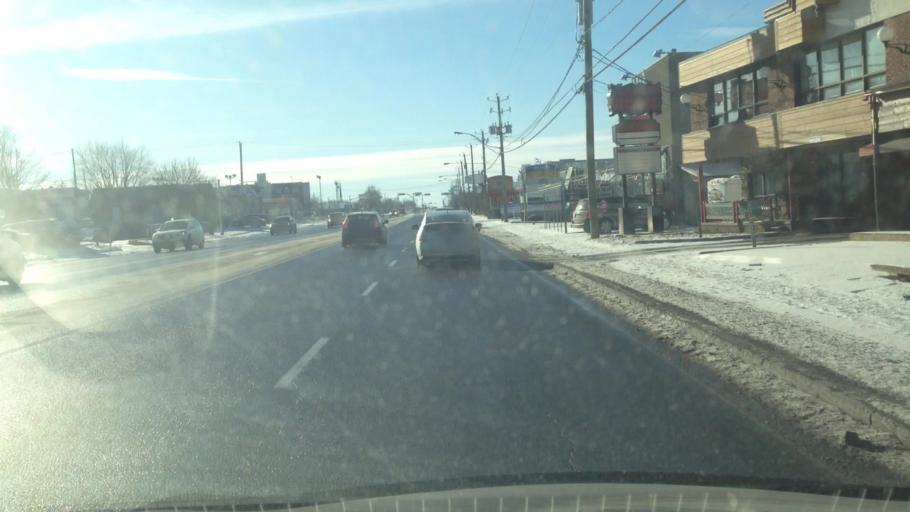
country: CA
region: Quebec
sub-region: Monteregie
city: Chateauguay
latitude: 45.3648
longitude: -73.7124
